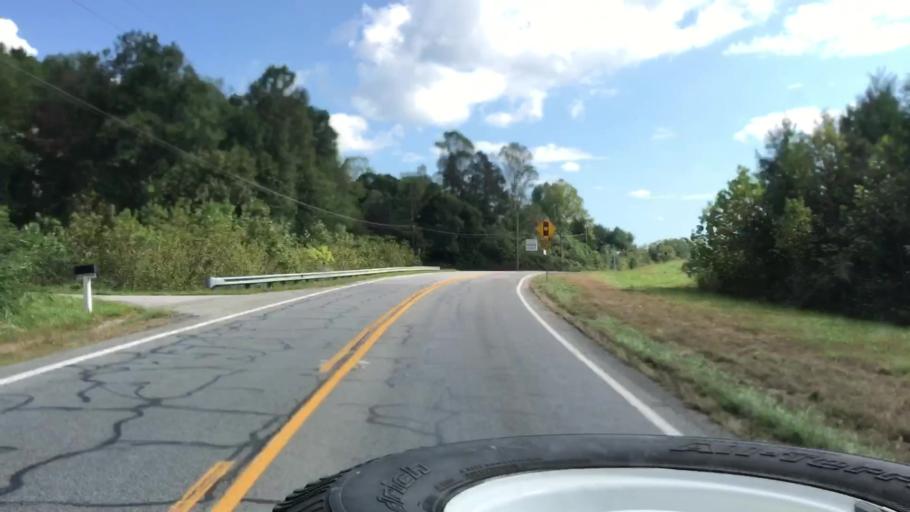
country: US
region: Georgia
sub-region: Fannin County
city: Blue Ridge
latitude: 34.8785
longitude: -84.3234
